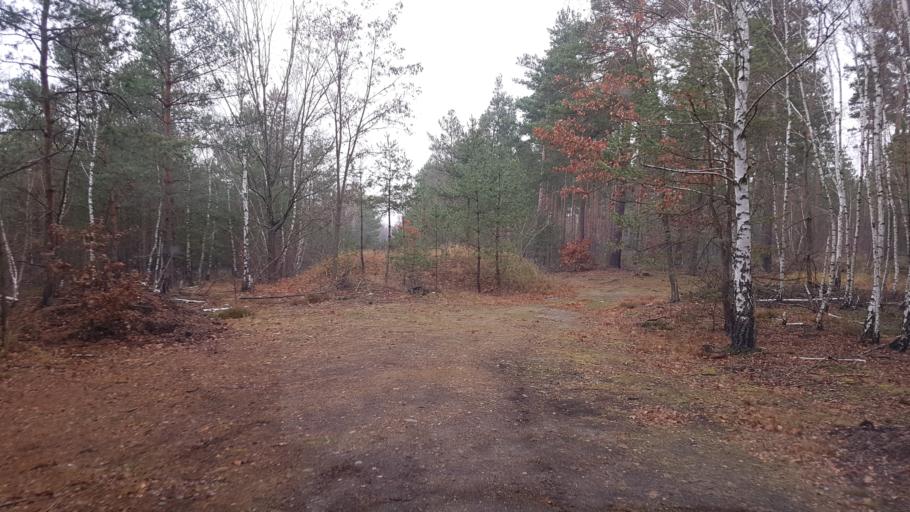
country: DE
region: Brandenburg
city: Sallgast
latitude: 51.5782
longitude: 13.8213
